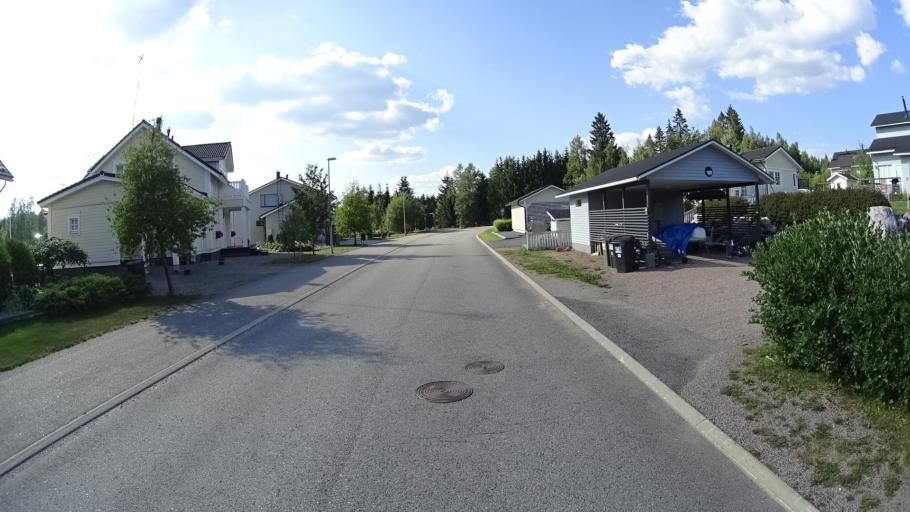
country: FI
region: Uusimaa
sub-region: Porvoo
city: Porvoo
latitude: 60.4130
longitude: 25.6561
